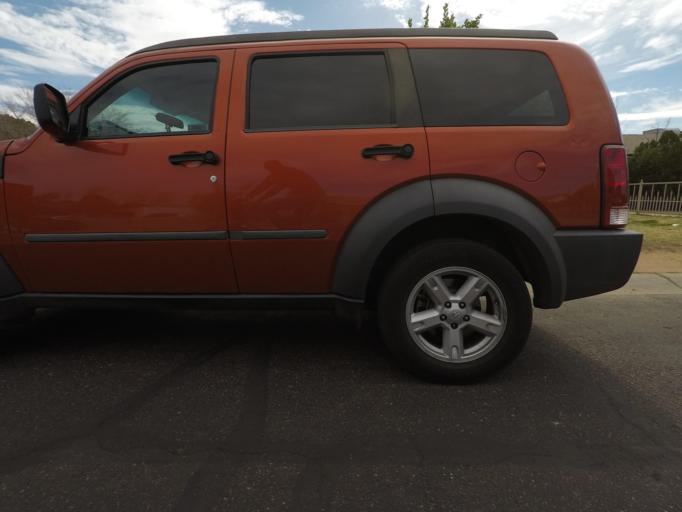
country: US
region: Arizona
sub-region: Maricopa County
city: Phoenix
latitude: 33.4768
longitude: -112.0063
